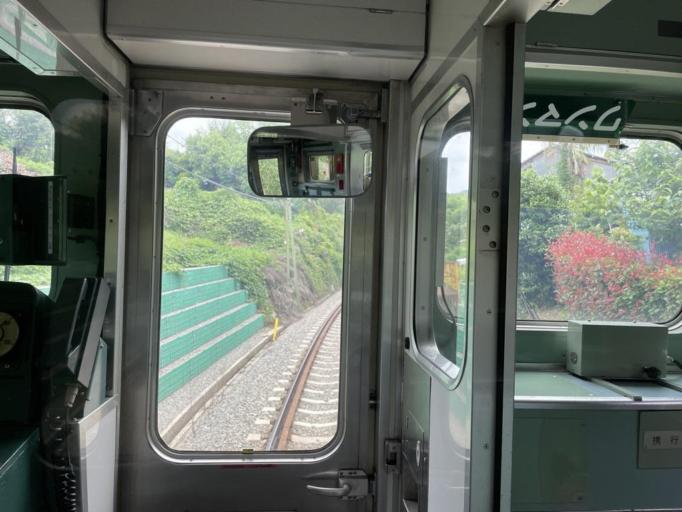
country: JP
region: Gunma
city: Tomioka
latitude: 36.2298
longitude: 138.7986
